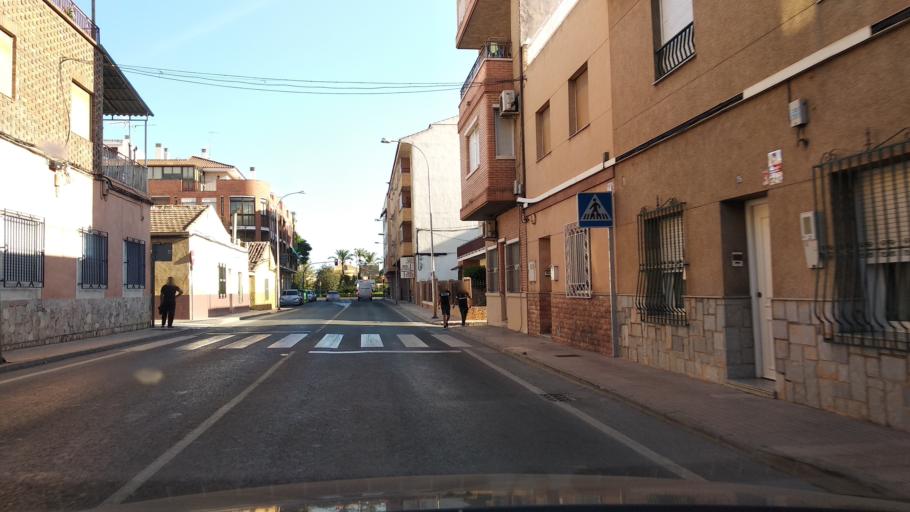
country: ES
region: Murcia
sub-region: Murcia
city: Santomera
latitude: 38.0604
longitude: -1.0525
